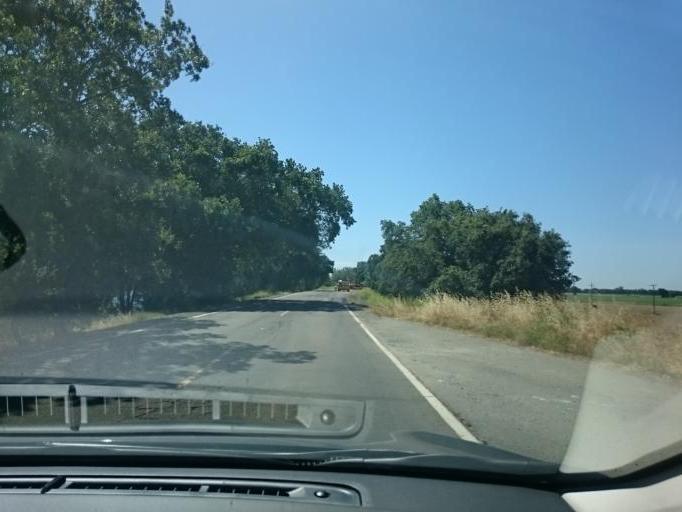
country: US
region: California
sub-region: Yolo County
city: West Sacramento
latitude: 38.4935
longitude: -121.5578
